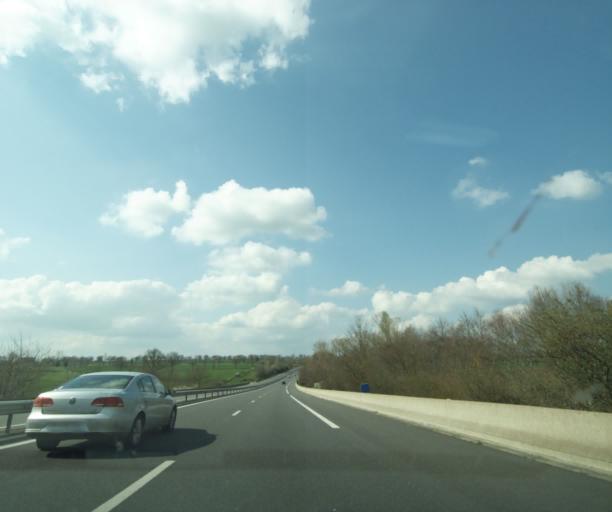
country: FR
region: Auvergne
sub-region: Departement de l'Allier
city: Montmarault
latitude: 46.3141
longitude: 2.9929
